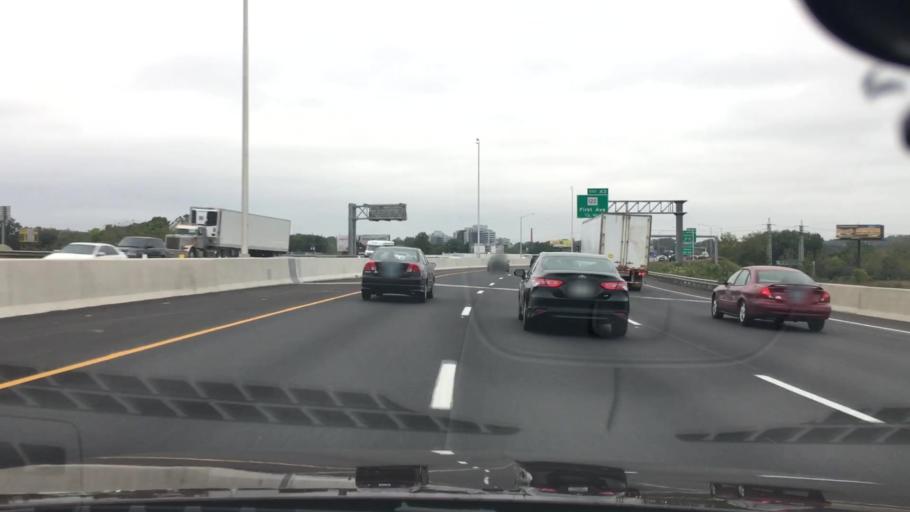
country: US
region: Connecticut
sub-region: New Haven County
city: West Haven
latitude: 41.2840
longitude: -72.9408
